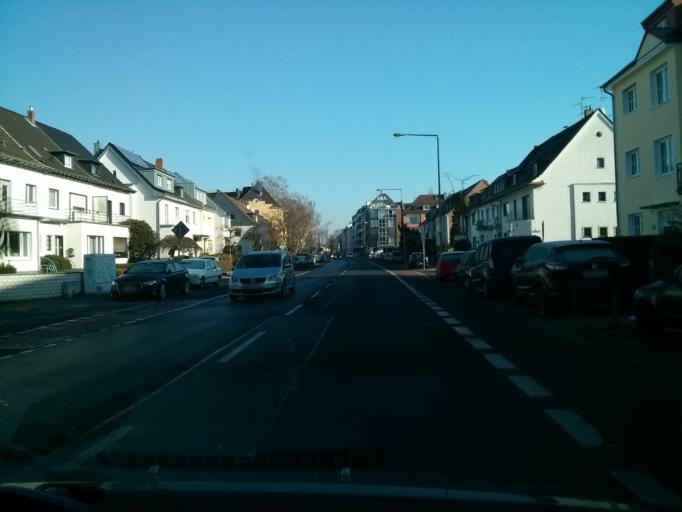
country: DE
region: North Rhine-Westphalia
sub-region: Regierungsbezirk Koln
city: Neustadt/Sued
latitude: 50.9107
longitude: 6.9175
